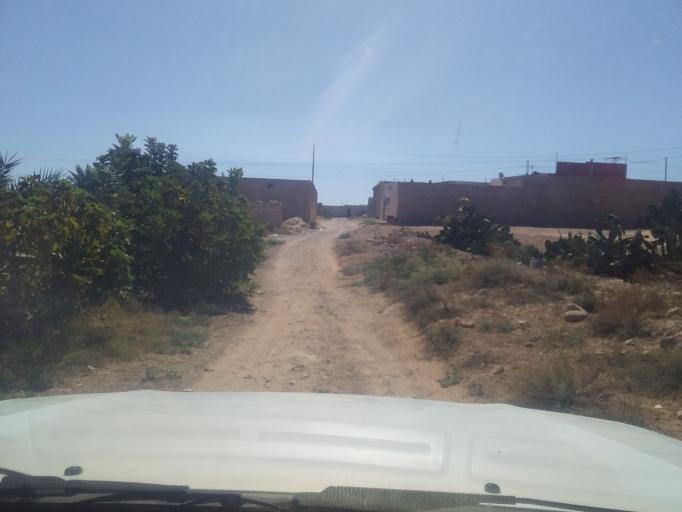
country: TN
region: Qabis
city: Matmata
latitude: 33.5833
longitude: 10.2800
